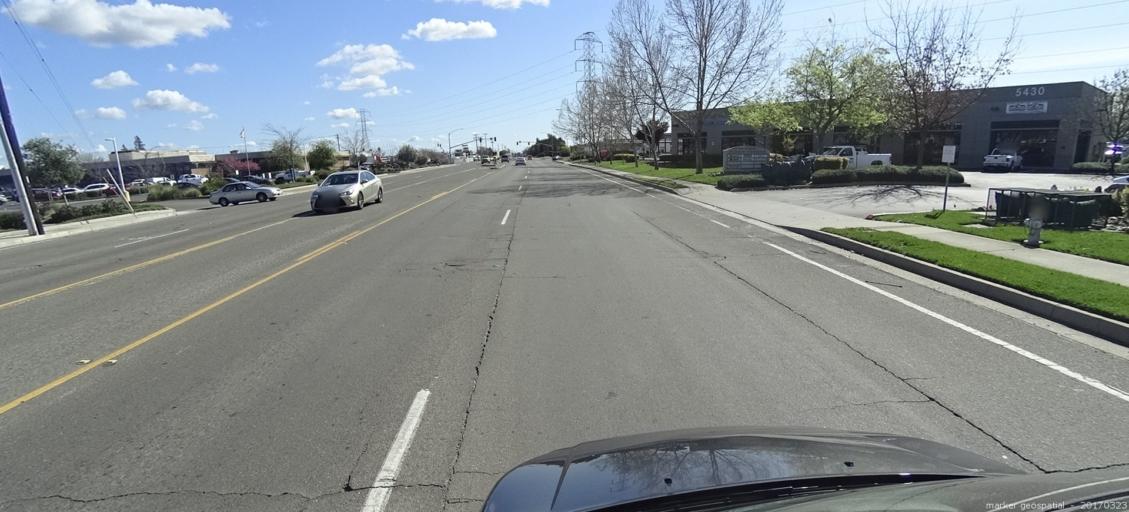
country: US
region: California
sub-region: Sacramento County
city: Florin
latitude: 38.5271
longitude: -121.3908
